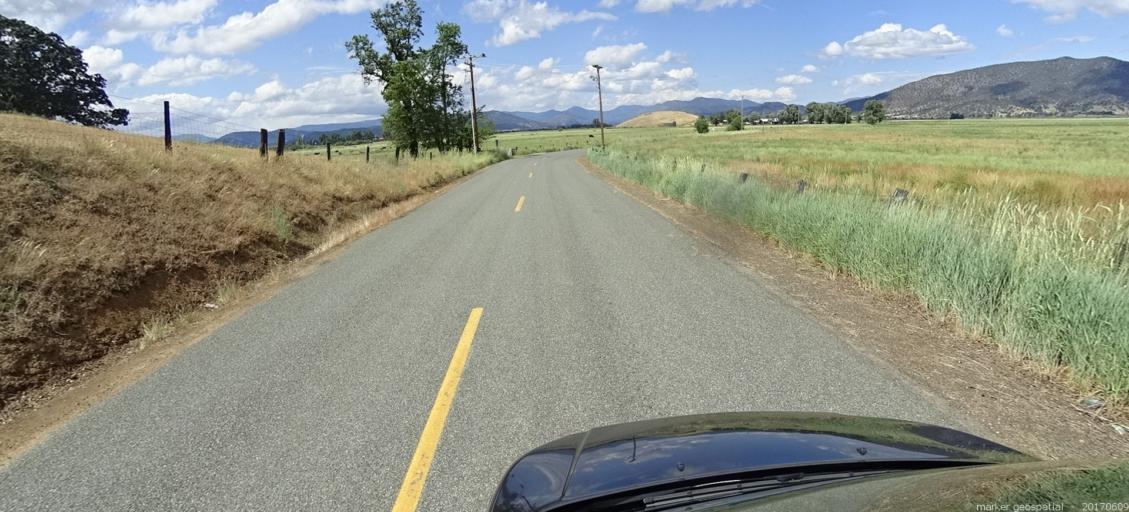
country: US
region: California
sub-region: Siskiyou County
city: Yreka
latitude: 41.4836
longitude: -122.8767
